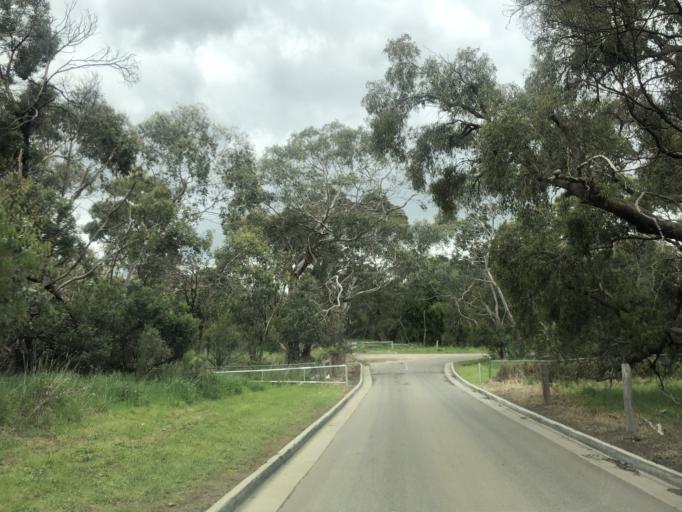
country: AU
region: Victoria
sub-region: Casey
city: Endeavour Hills
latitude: -37.9611
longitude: 145.2435
